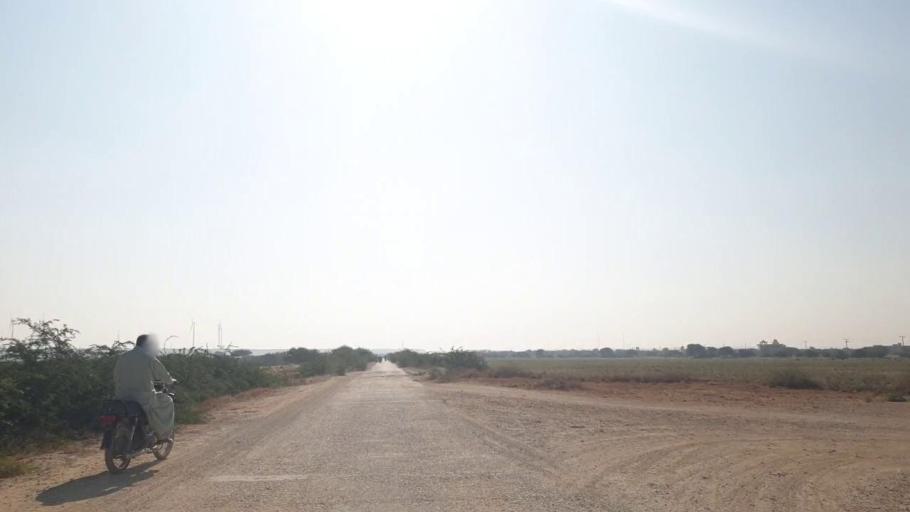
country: PK
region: Sindh
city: Thatta
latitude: 25.1334
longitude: 67.7736
